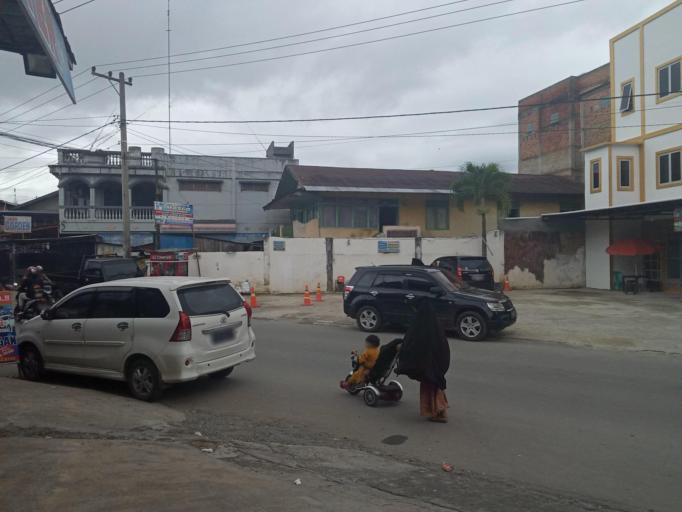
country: ID
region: Jambi
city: Sungai Penuh
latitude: -2.0685
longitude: 101.3999
